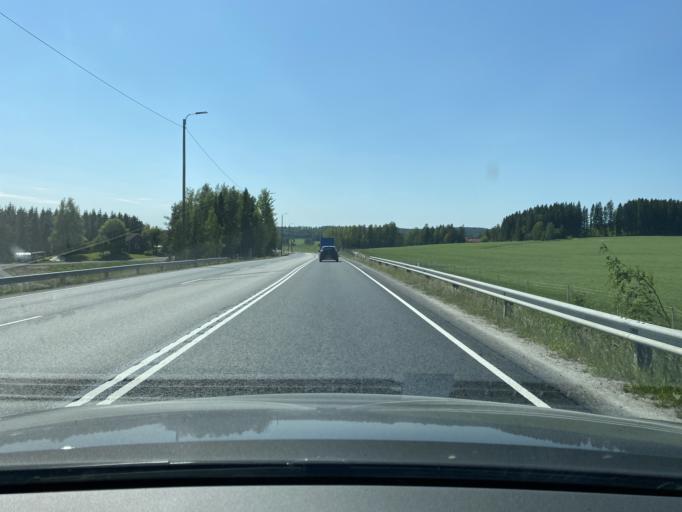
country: FI
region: Pirkanmaa
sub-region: Lounais-Pirkanmaa
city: Mouhijaervi
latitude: 61.3673
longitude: 23.1172
